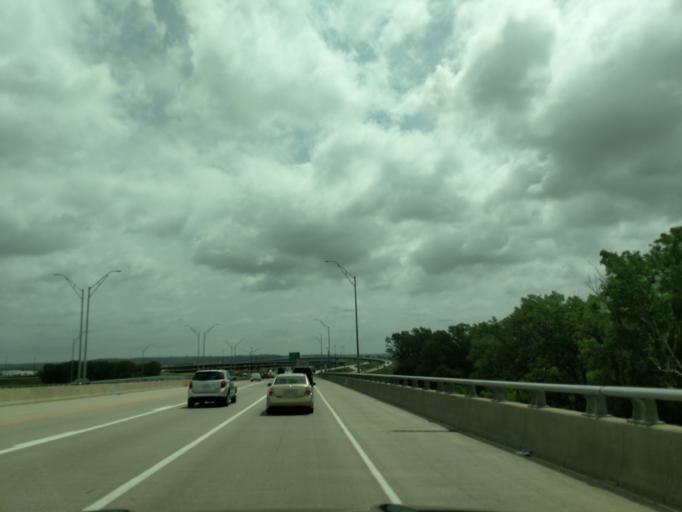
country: US
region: Nebraska
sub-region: Douglas County
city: Omaha
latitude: 41.2317
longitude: -95.9094
